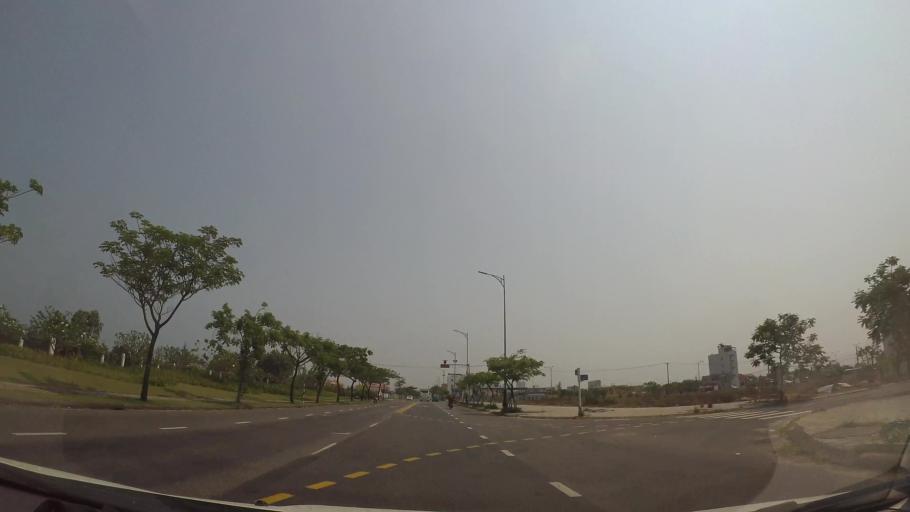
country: VN
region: Da Nang
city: Ngu Hanh Son
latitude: 15.9877
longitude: 108.2720
